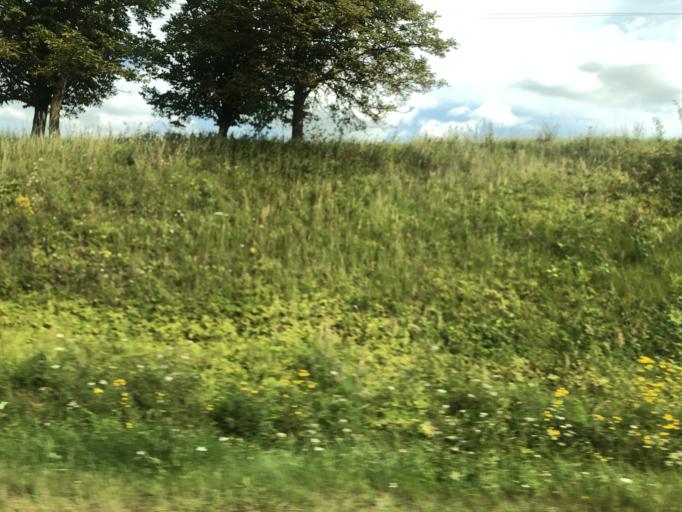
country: LV
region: Vecumnieki
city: Vecumnieki
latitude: 56.4787
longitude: 24.5870
